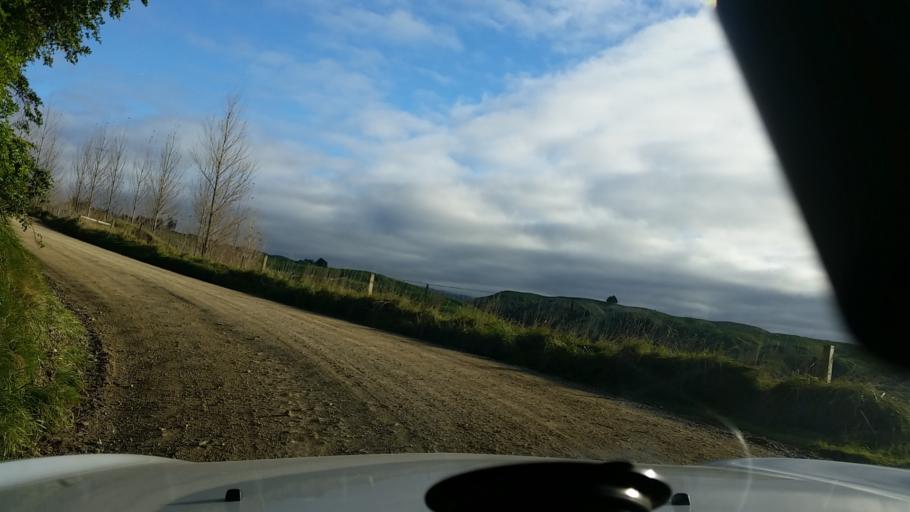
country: NZ
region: Hawke's Bay
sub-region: Napier City
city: Napier
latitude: -39.2616
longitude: 176.8518
